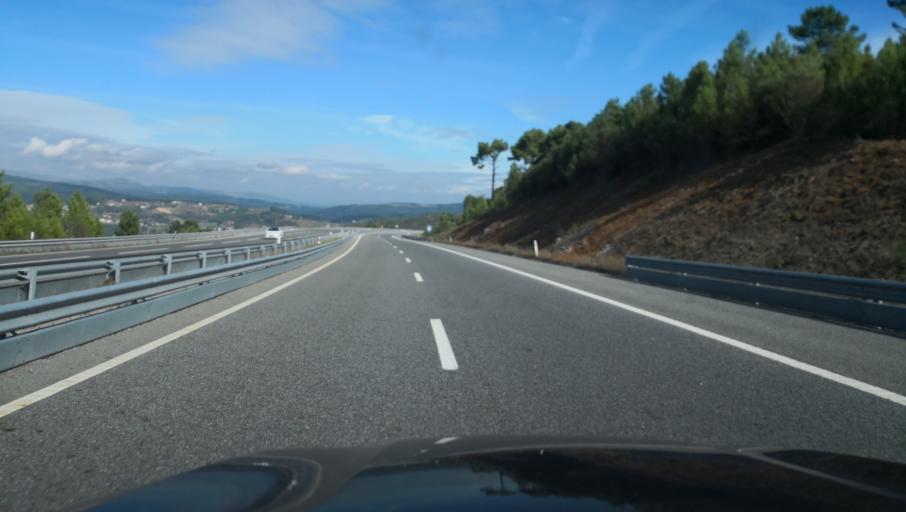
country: PT
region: Vila Real
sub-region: Boticas
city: Boticas
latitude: 41.6178
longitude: -7.6061
